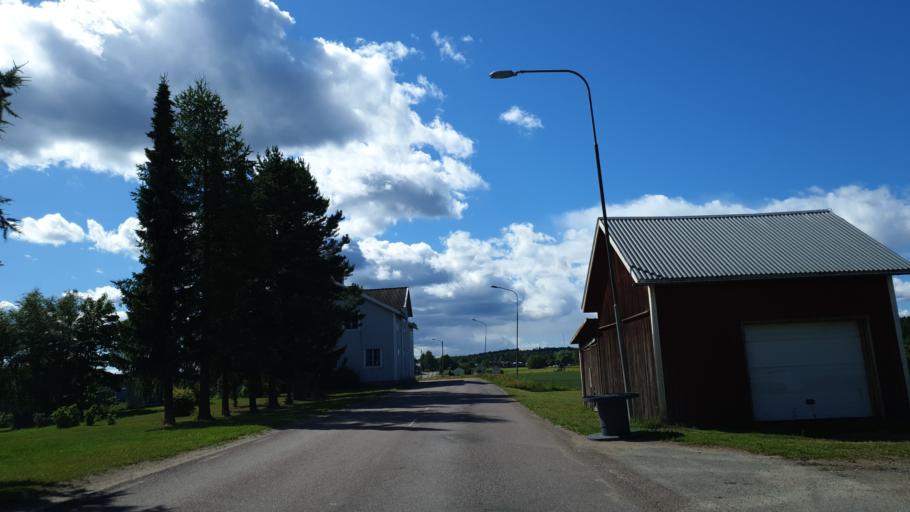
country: SE
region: Gaevleborg
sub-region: Nordanstigs Kommun
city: Bergsjoe
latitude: 62.0513
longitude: 17.2143
